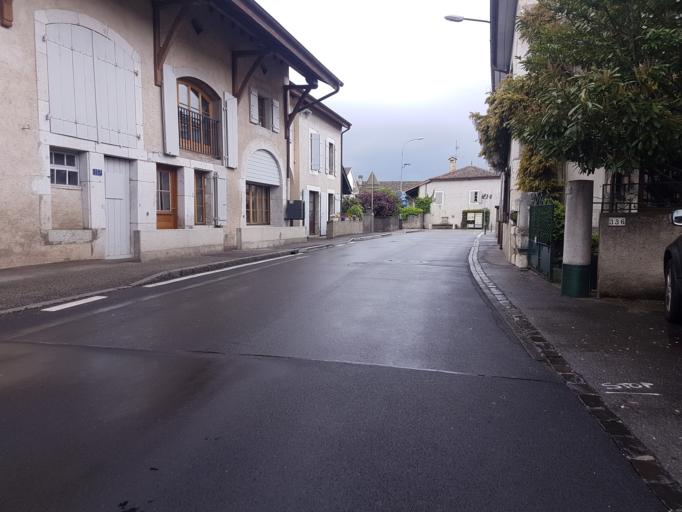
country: CH
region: Geneva
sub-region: Geneva
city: Dardagny
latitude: 46.1881
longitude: 6.0137
